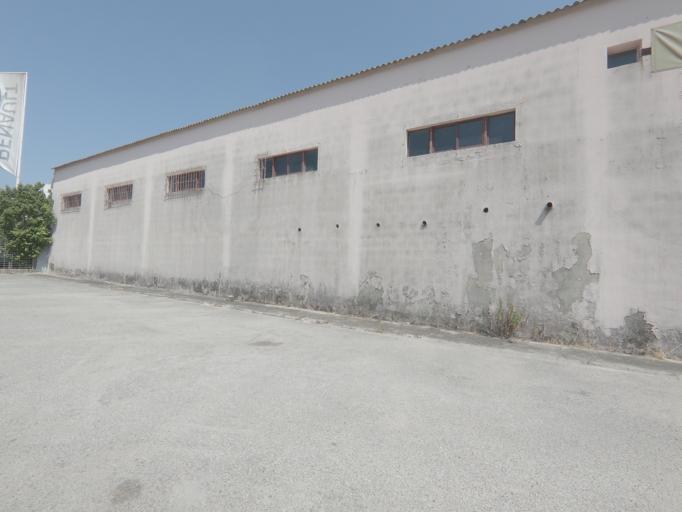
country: PT
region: Setubal
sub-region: Palmela
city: Palmela
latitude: 38.5501
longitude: -8.8858
